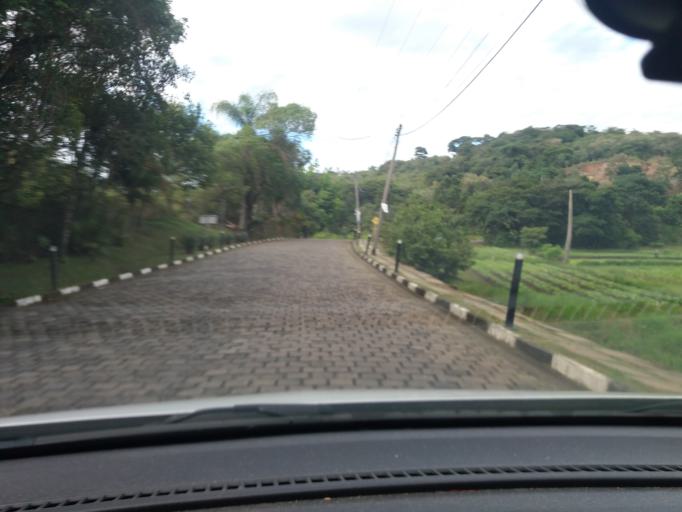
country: BR
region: Sao Paulo
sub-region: Bom Jesus Dos Perdoes
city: Bom Jesus dos Perdoes
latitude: -23.1637
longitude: -46.4533
